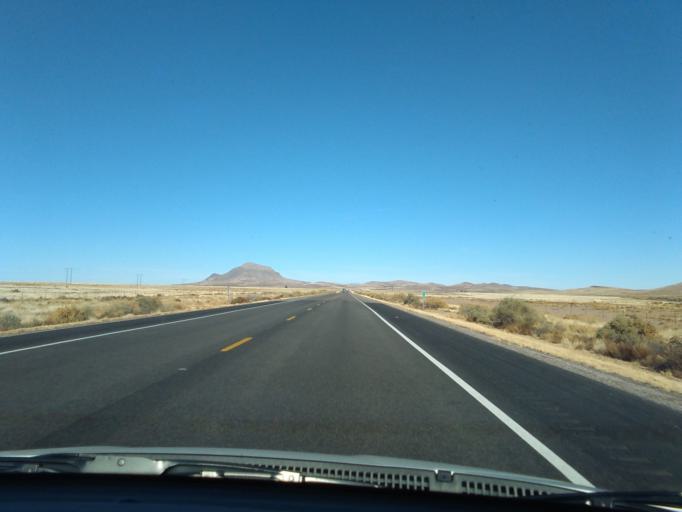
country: US
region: New Mexico
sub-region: Dona Ana County
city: Hatch
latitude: 32.5448
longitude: -107.4806
